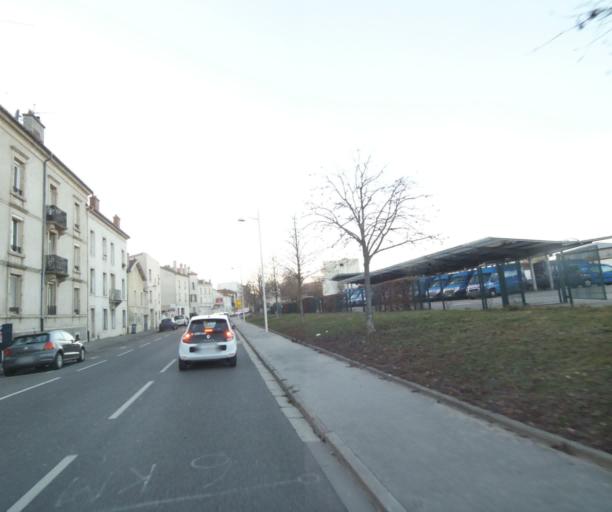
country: FR
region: Lorraine
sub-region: Departement de Meurthe-et-Moselle
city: Malzeville
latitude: 48.7013
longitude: 6.1843
